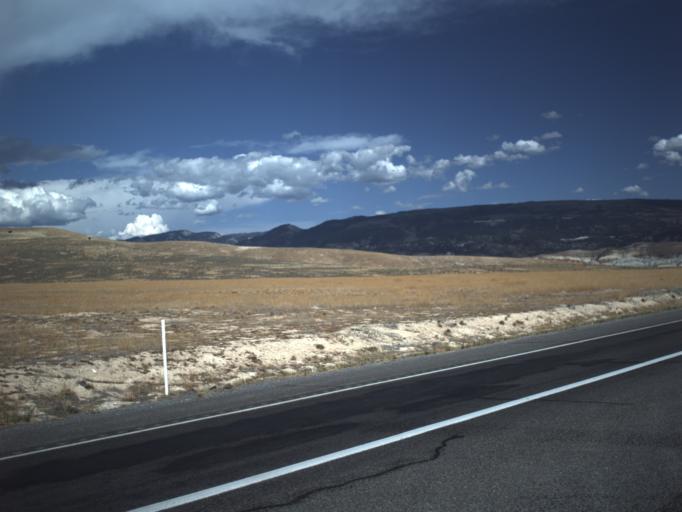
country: US
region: Utah
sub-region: Sanpete County
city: Gunnison
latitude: 39.1591
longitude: -111.7821
